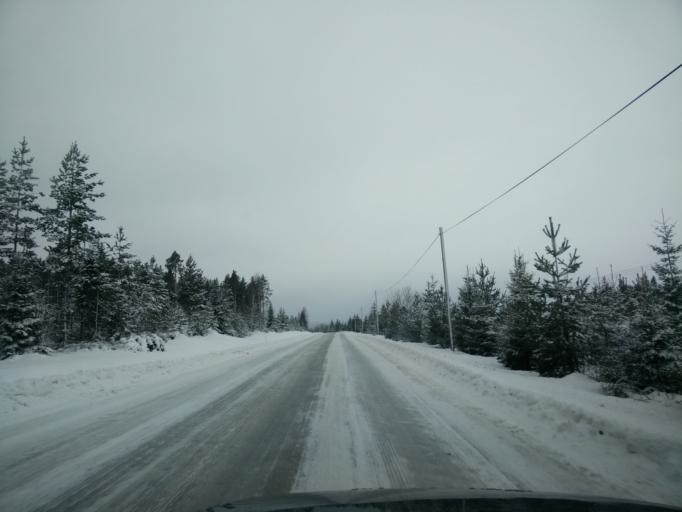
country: SE
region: Vaesternorrland
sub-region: Ange Kommun
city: Ange
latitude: 62.3986
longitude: 15.3496
